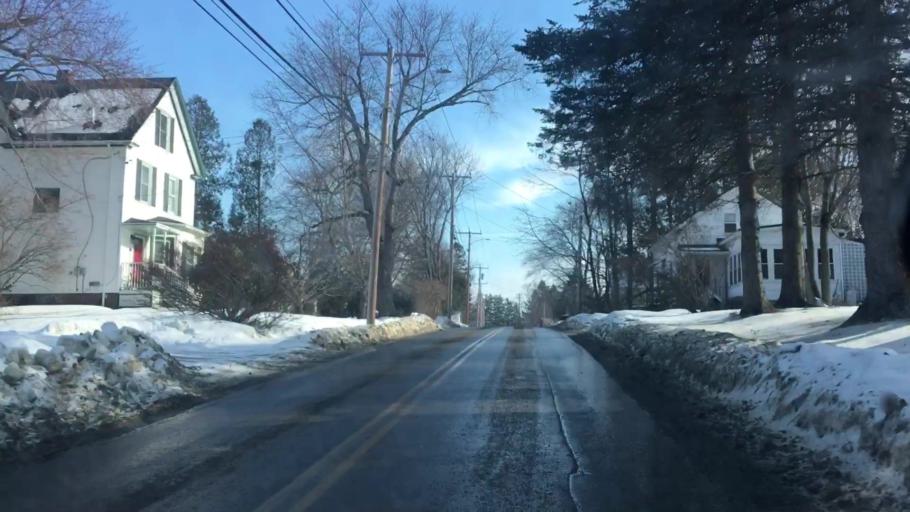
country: US
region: Maine
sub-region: Penobscot County
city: Brewer
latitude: 44.7687
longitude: -68.7762
